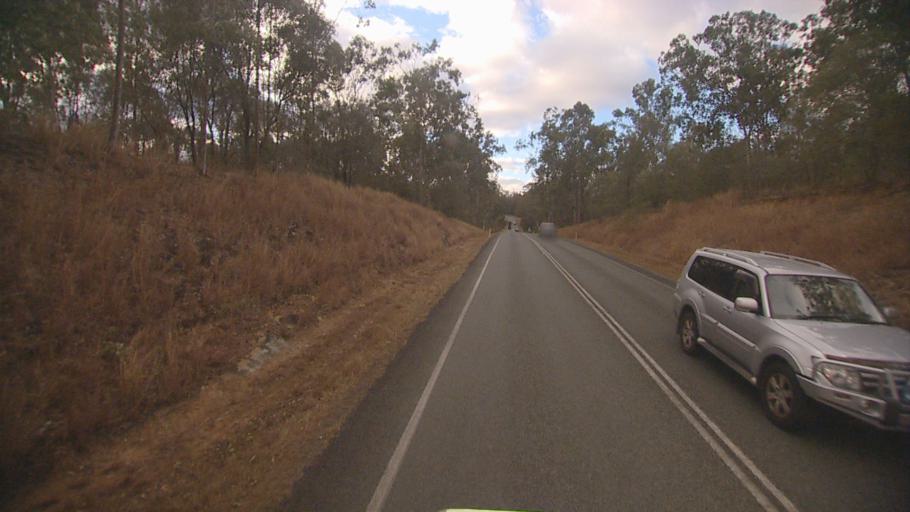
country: AU
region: Queensland
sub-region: Logan
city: Cedar Vale
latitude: -27.9073
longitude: 153.0900
